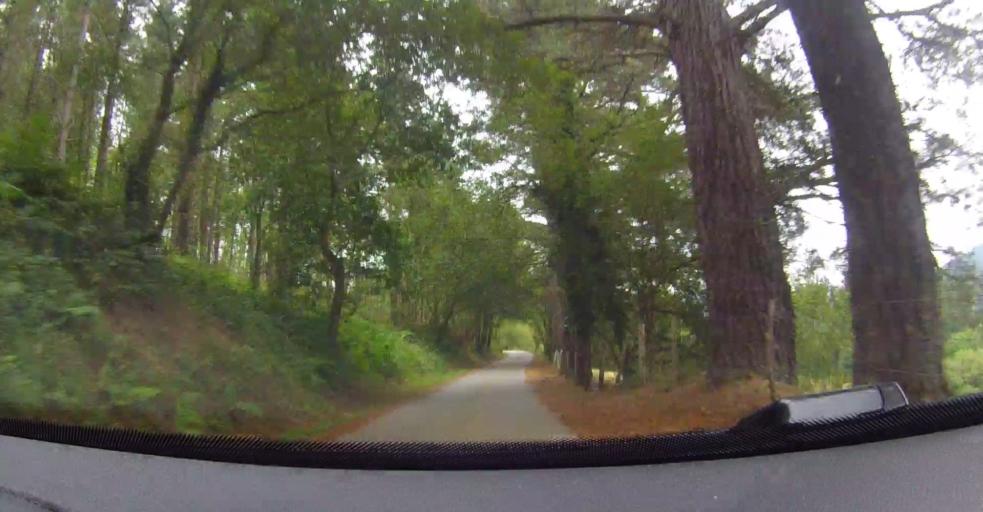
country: ES
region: Basque Country
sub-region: Bizkaia
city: Urrestieta
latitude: 43.2312
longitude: -3.1778
